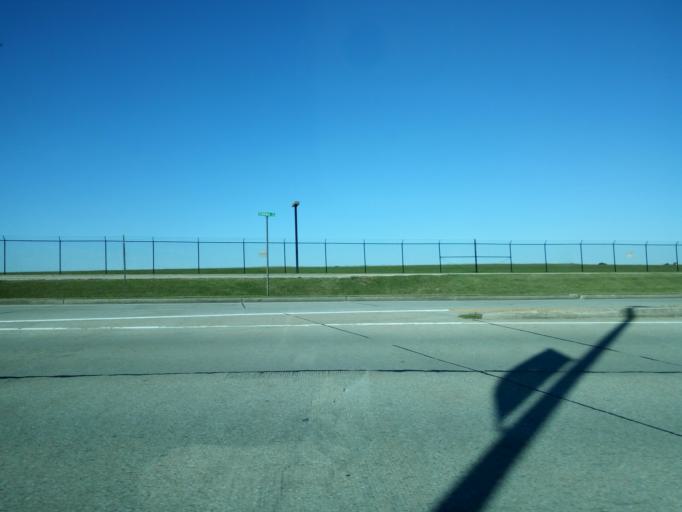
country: US
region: Kentucky
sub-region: Jefferson County
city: Audubon Park
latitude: 38.1871
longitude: -85.7465
